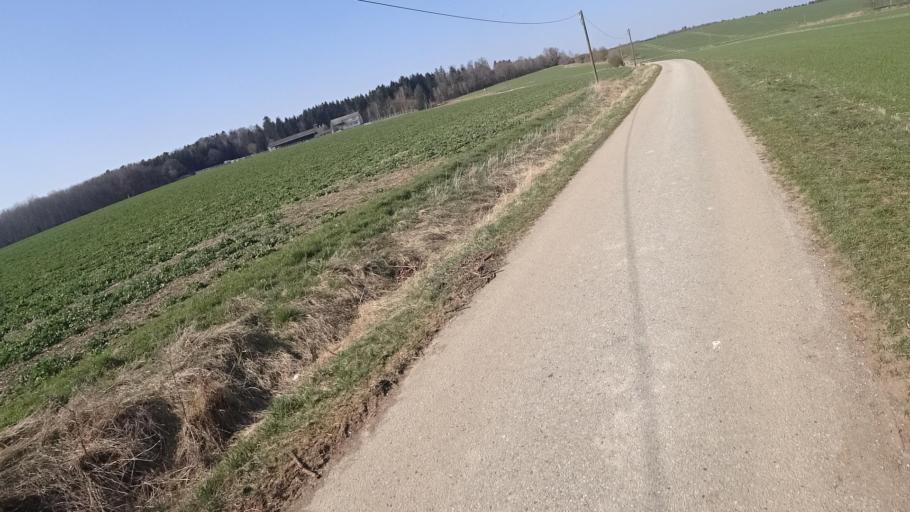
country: DE
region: Rheinland-Pfalz
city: Rheinbollen
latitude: 50.0153
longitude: 7.6639
